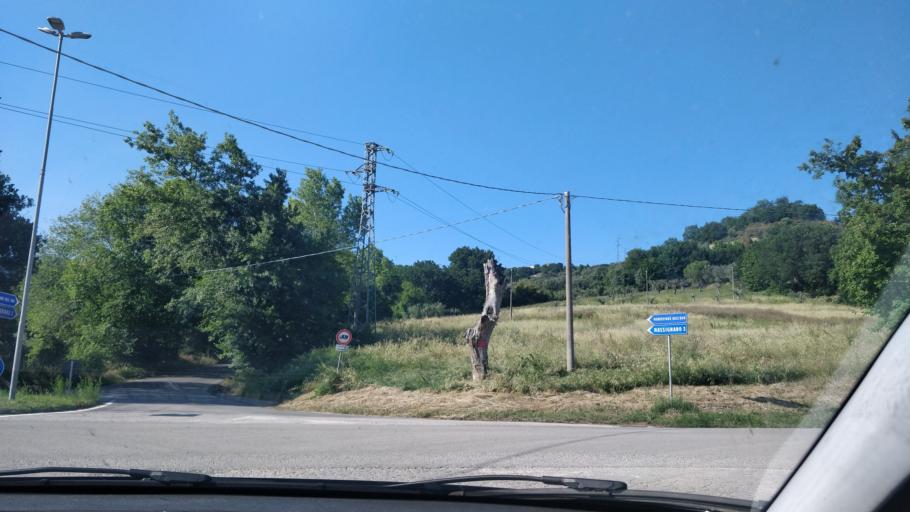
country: IT
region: The Marches
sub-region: Provincia di Ascoli Piceno
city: Massignano
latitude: 43.0371
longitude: 13.8005
